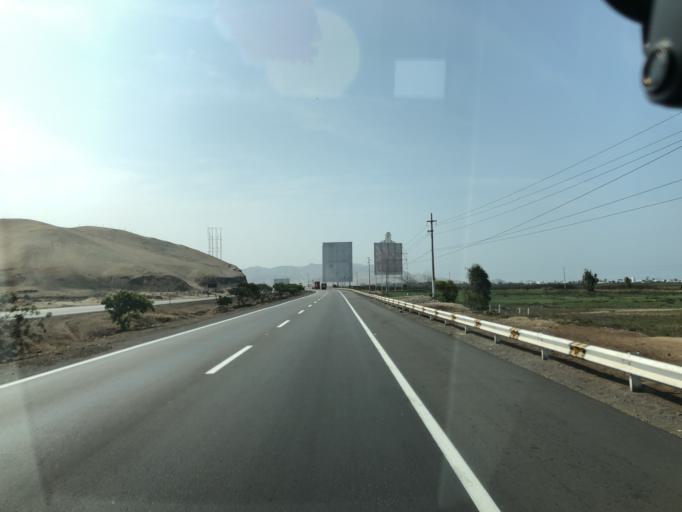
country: PE
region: Lima
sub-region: Provincia de Canete
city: Chilca
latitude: -12.5565
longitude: -76.7107
